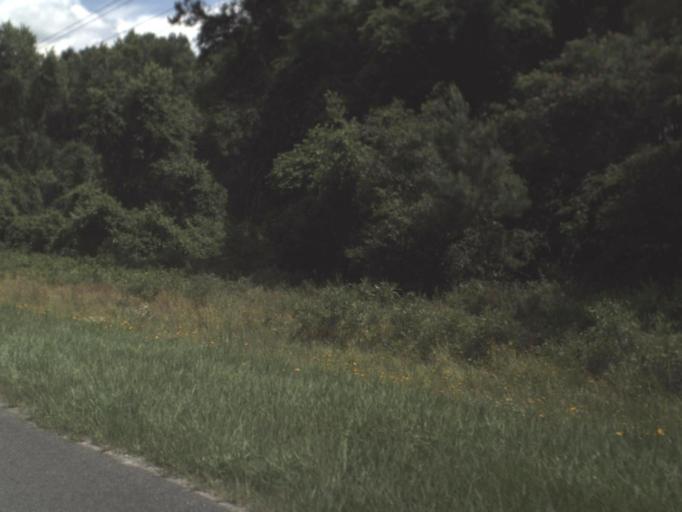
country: US
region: Florida
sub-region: Alachua County
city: High Springs
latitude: 29.8844
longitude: -82.6678
